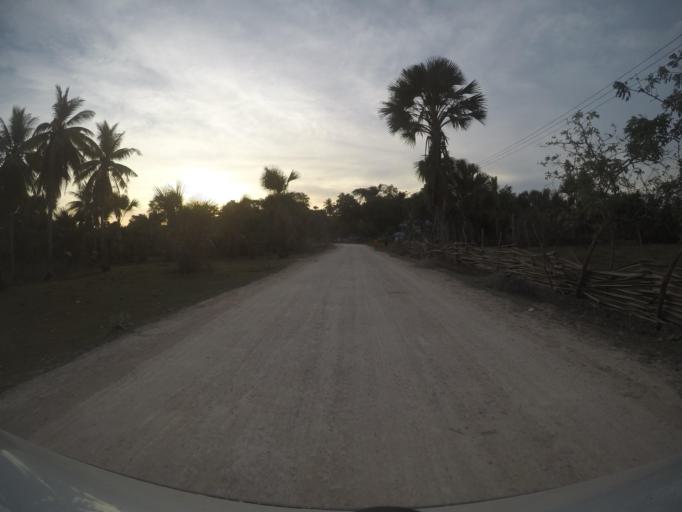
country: TL
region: Viqueque
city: Viqueque
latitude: -8.9400
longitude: 126.4428
